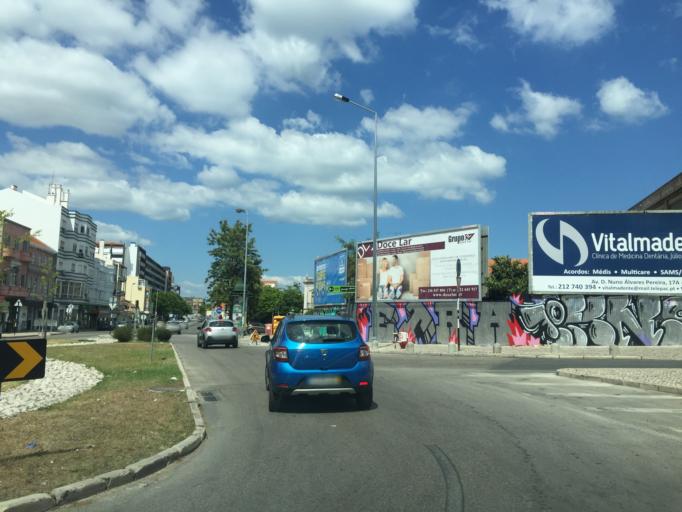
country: PT
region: Setubal
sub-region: Almada
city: Piedade
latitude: 38.6695
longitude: -9.1588
